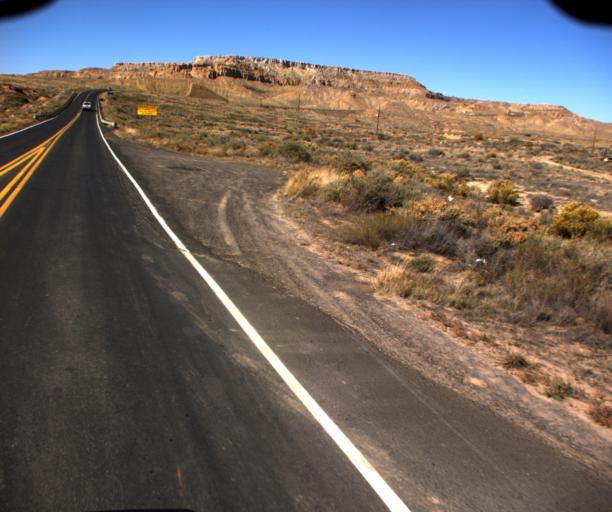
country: US
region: Arizona
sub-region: Navajo County
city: First Mesa
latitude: 35.7936
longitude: -110.5065
